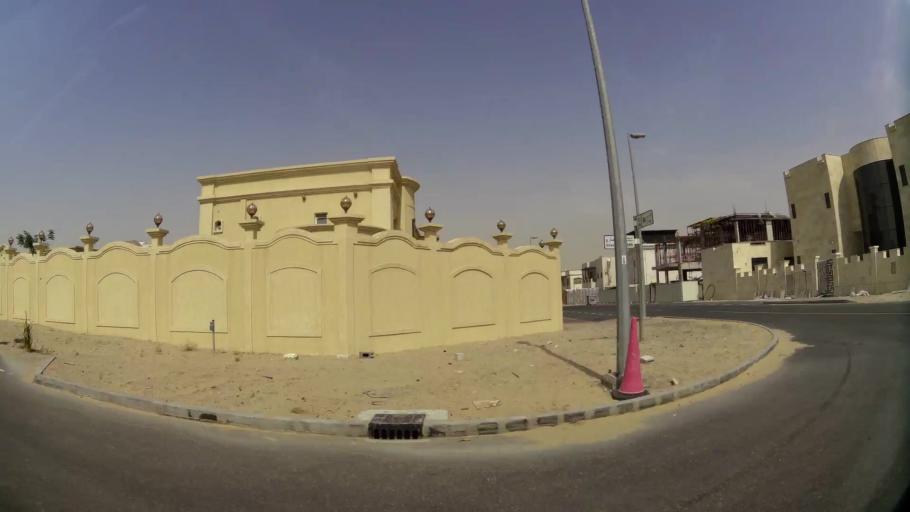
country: AE
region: Ash Shariqah
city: Sharjah
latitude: 25.2569
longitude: 55.4643
